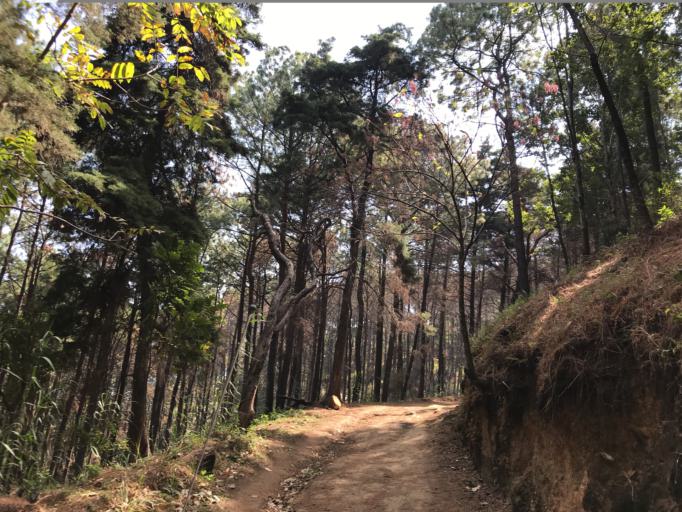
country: GT
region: Guatemala
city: Petapa
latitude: 14.4837
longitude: -90.5544
